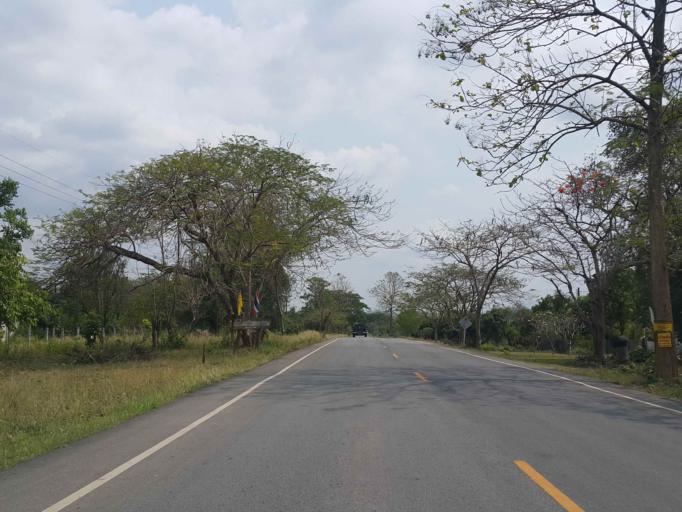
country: TH
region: Lampang
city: Thoen
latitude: 17.5097
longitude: 99.3506
